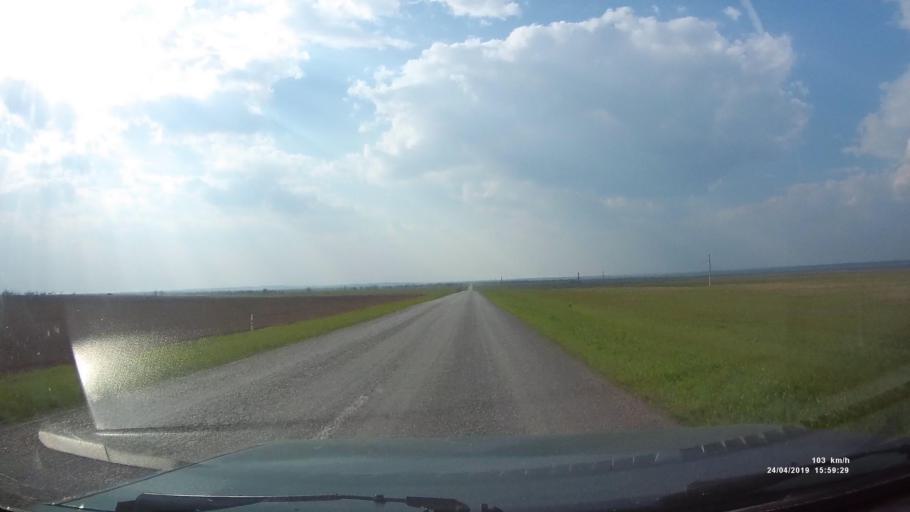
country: RU
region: Rostov
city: Sovetskoye
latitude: 46.6238
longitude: 42.4712
